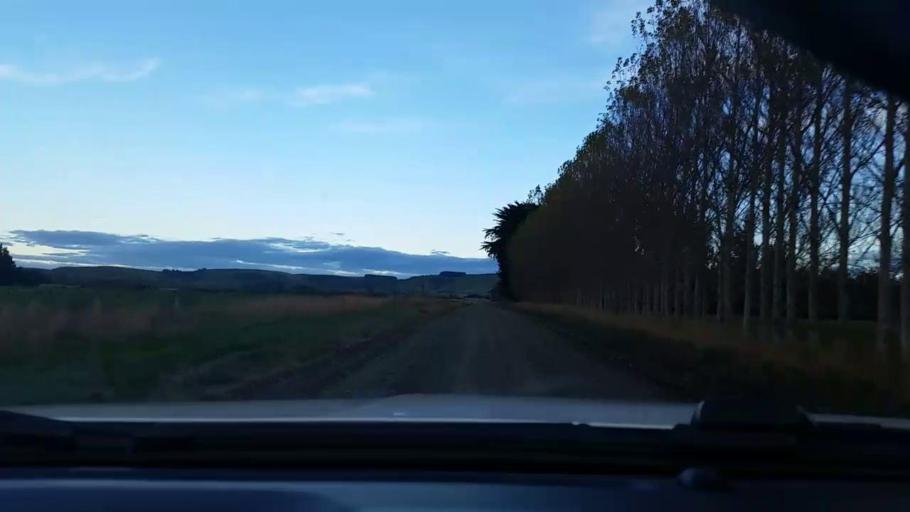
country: NZ
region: Southland
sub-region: Southland District
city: Winton
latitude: -46.1055
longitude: 168.4537
